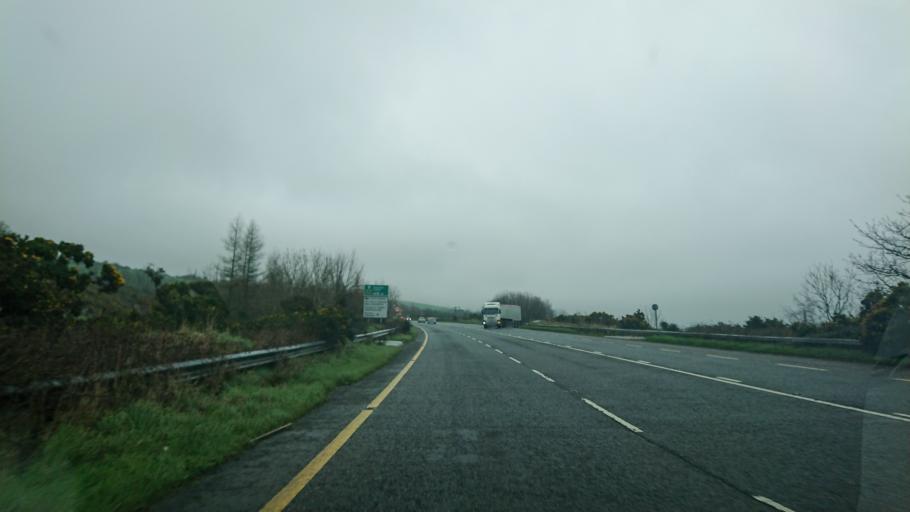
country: IE
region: Munster
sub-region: County Cork
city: Kinsale
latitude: 51.8108
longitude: -8.5407
